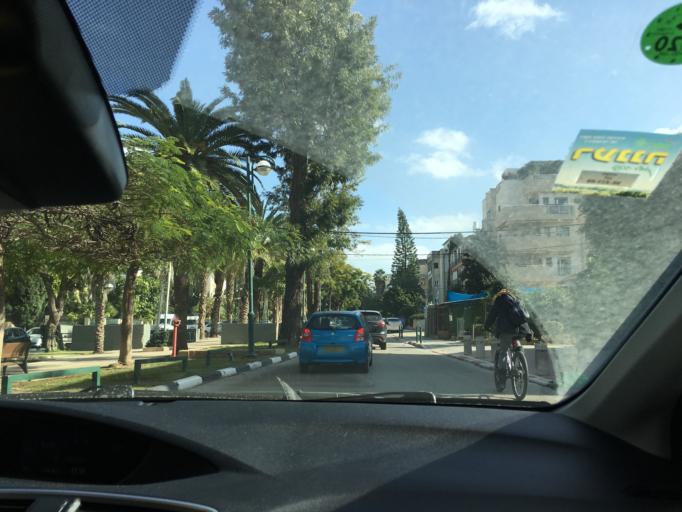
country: IL
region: Tel Aviv
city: Ramat HaSharon
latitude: 32.1456
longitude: 34.8389
